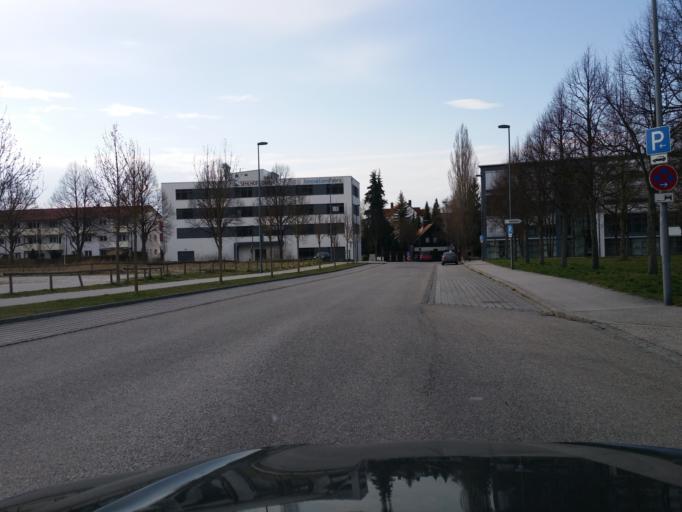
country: DE
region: Bavaria
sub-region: Lower Bavaria
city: Ergolding
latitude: 48.5498
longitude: 12.1857
